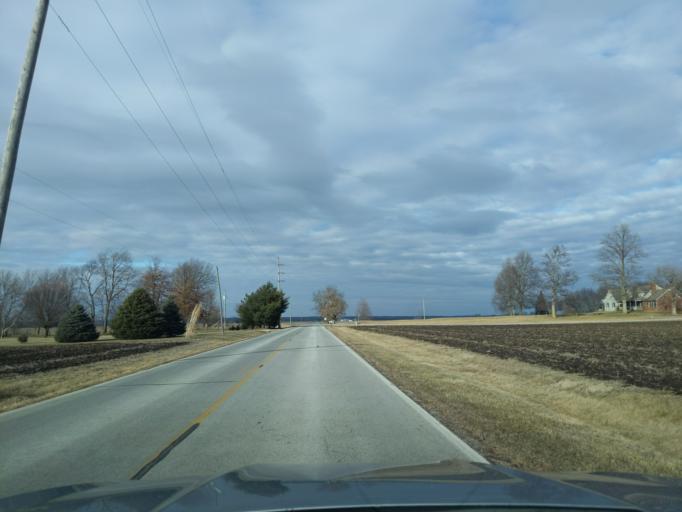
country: US
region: Indiana
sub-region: Tippecanoe County
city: Shadeland
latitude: 40.3509
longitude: -86.9755
